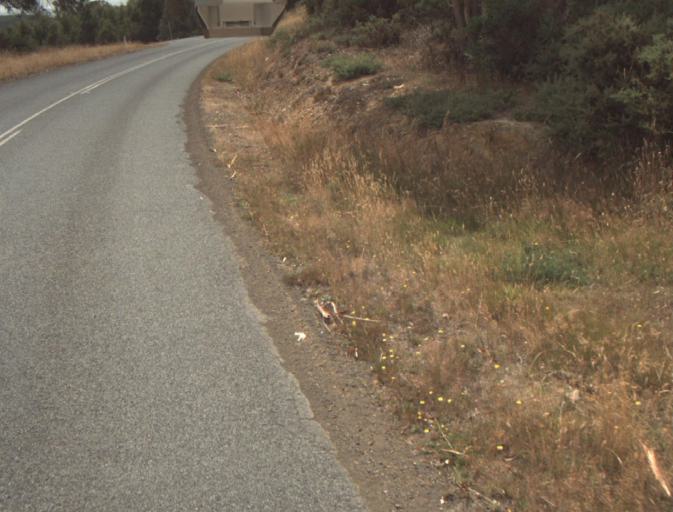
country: AU
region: Tasmania
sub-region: Northern Midlands
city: Evandale
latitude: -41.4828
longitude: 147.5038
